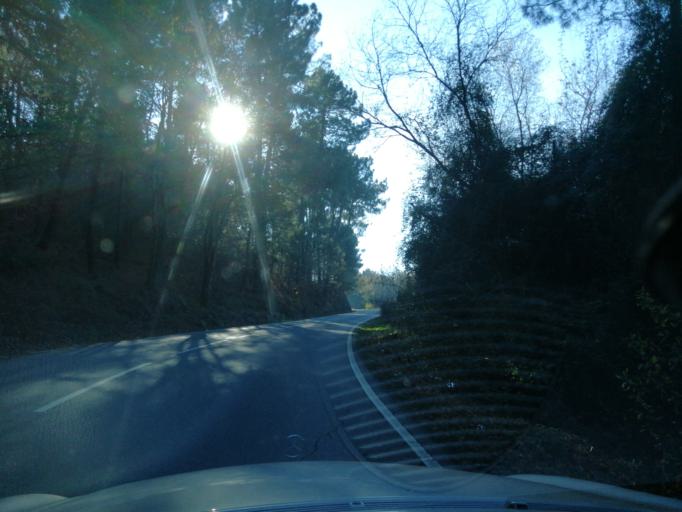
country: PT
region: Braga
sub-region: Braga
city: Adaufe
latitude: 41.5747
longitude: -8.3878
